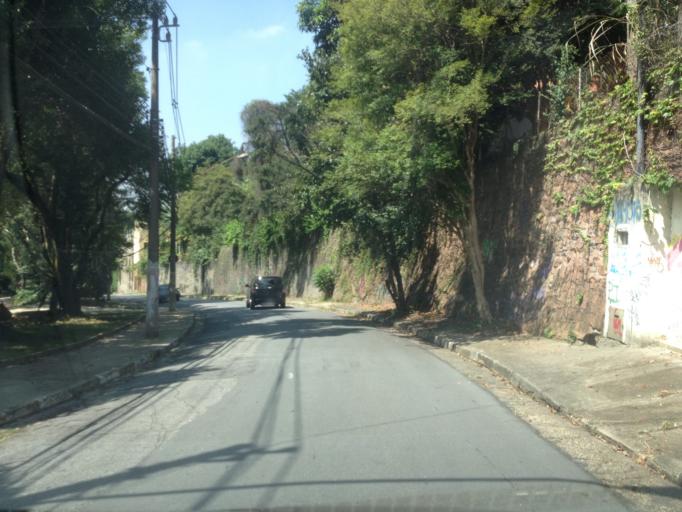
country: BR
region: Sao Paulo
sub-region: Sao Paulo
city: Sao Paulo
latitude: -23.5440
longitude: -46.6809
